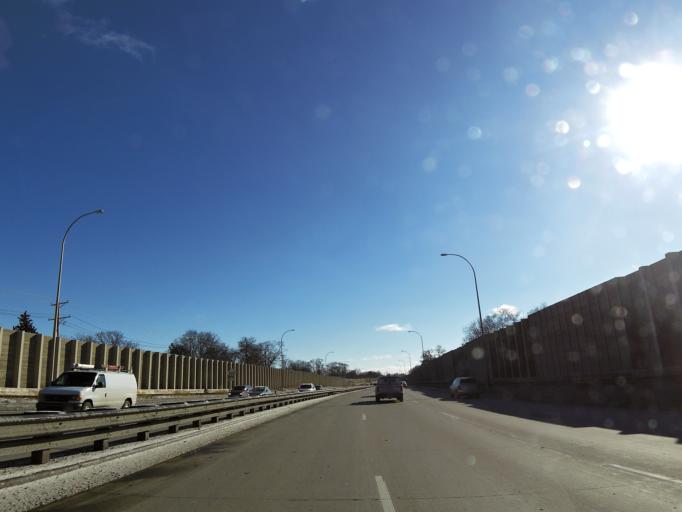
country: US
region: Minnesota
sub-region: Hennepin County
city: Saint Louis Park
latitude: 44.9264
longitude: -93.3495
